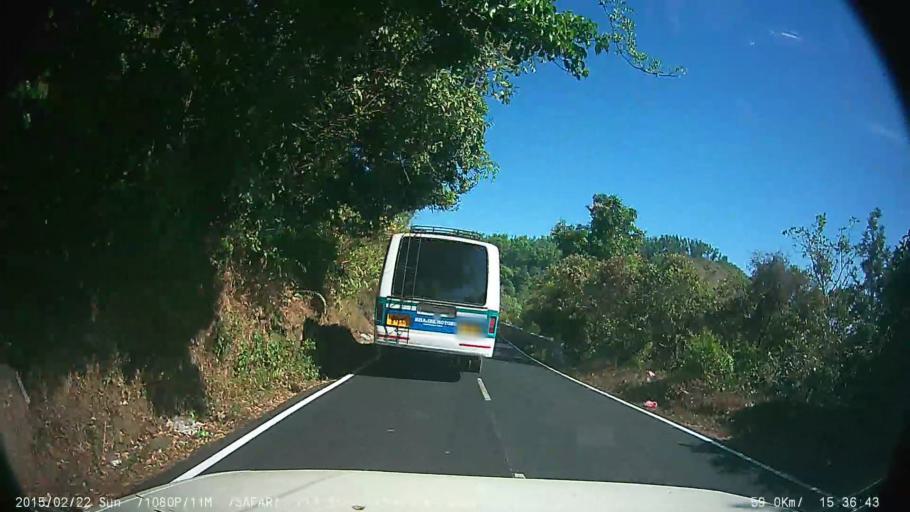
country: IN
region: Kerala
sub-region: Kottayam
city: Erattupetta
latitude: 9.5612
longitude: 76.9797
